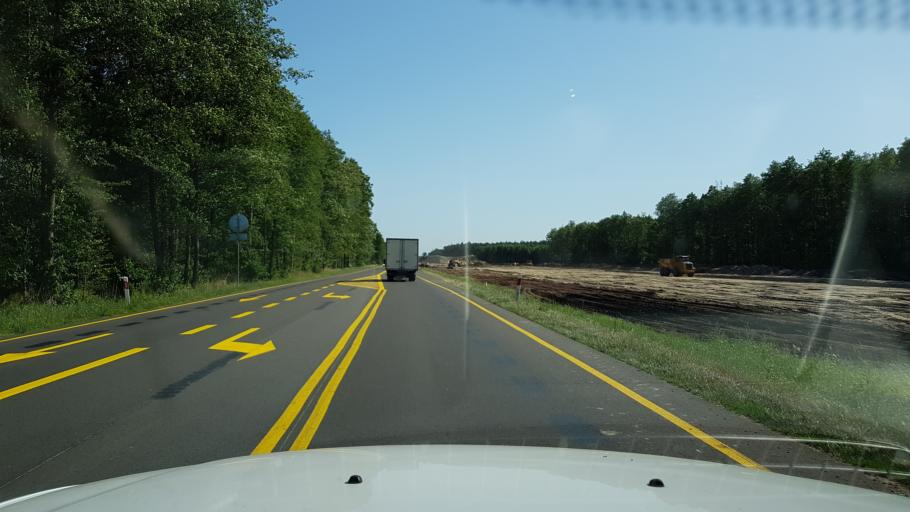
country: PL
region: West Pomeranian Voivodeship
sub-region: Powiat goleniowski
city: Przybiernow
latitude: 53.6661
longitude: 14.8147
